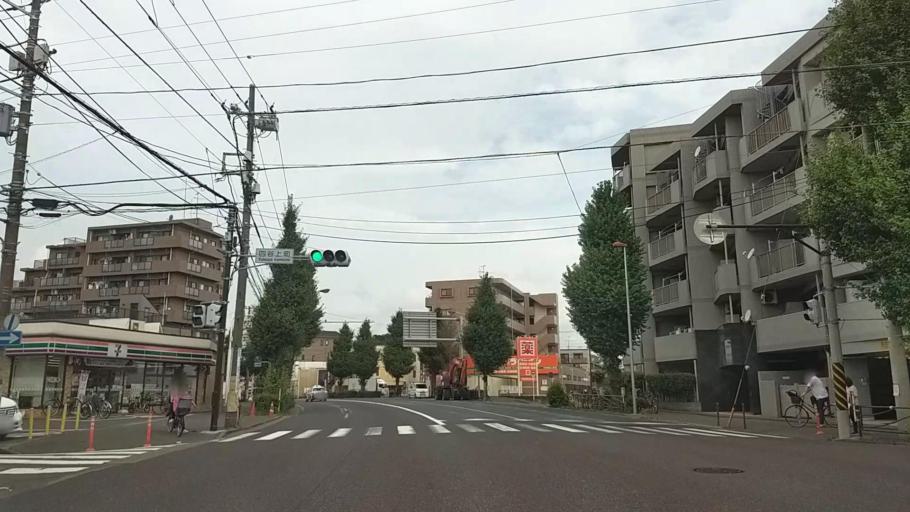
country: JP
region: Kanagawa
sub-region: Kawasaki-shi
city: Kawasaki
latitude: 35.5296
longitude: 139.7358
